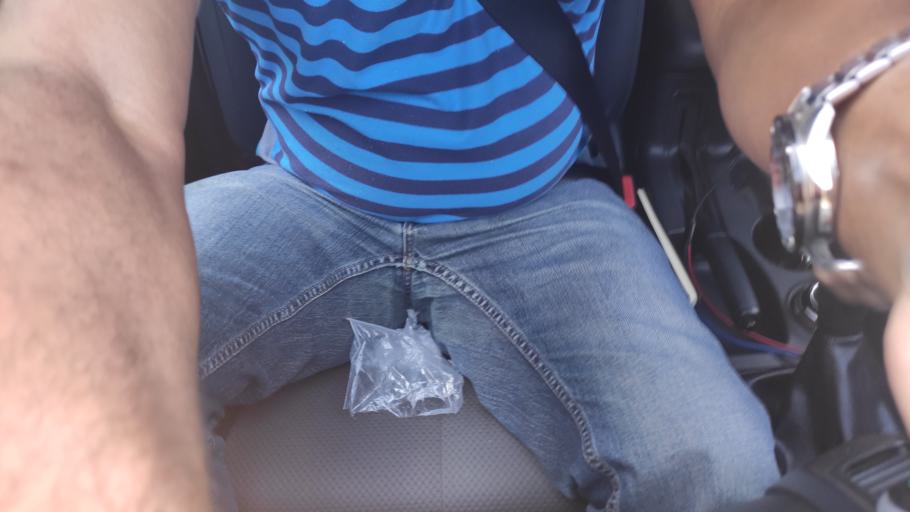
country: CV
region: Mosteiros
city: Porto dos Mosteiros
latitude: 15.0193
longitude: -24.3951
